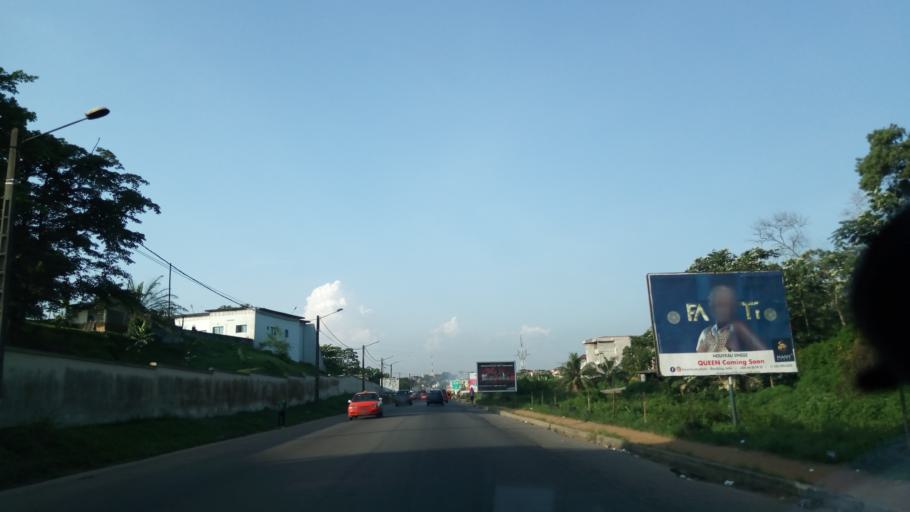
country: CI
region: Lagunes
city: Abobo
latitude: 5.3813
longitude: -4.0066
